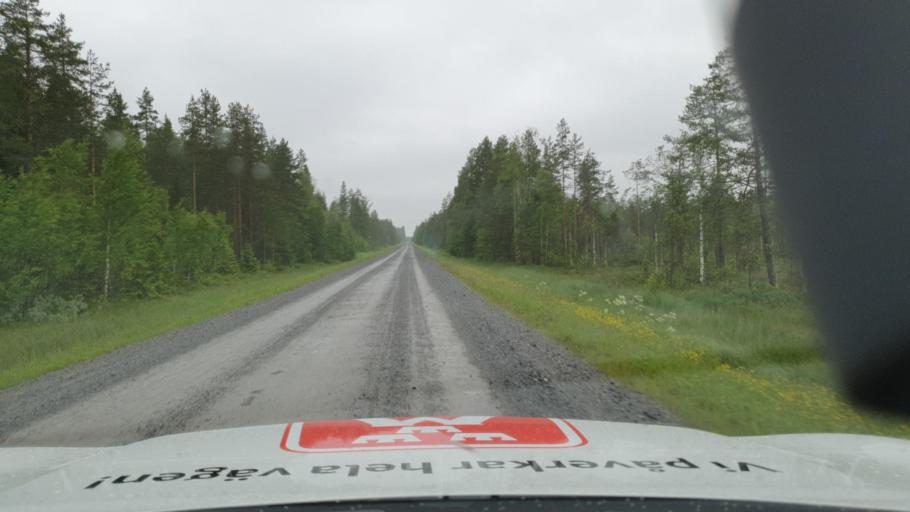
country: SE
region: Vaesterbotten
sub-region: Nordmalings Kommun
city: Nordmaling
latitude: 63.8216
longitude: 19.4935
